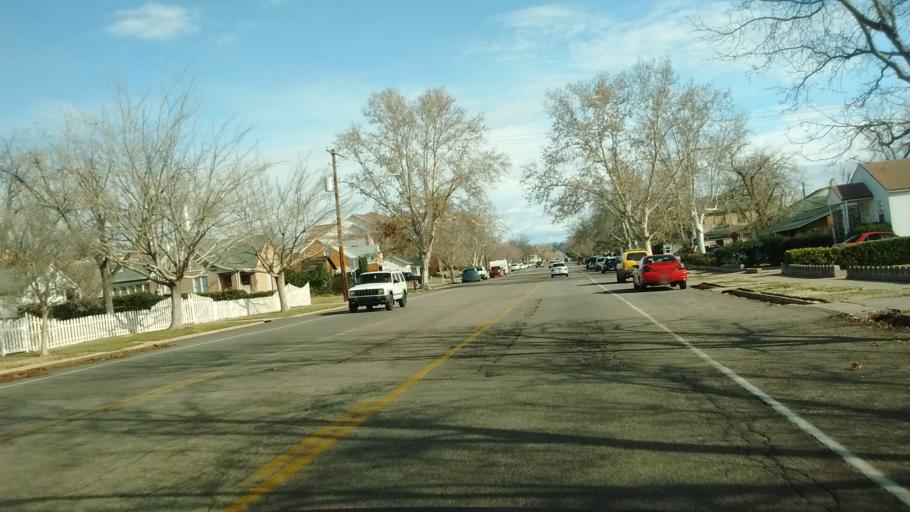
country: US
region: Utah
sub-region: Washington County
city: Saint George
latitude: 37.1065
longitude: -113.5871
